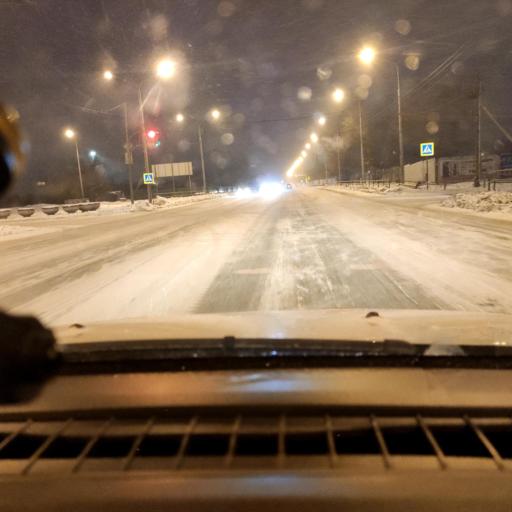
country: RU
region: Samara
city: Otradnyy
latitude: 53.3603
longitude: 51.3468
